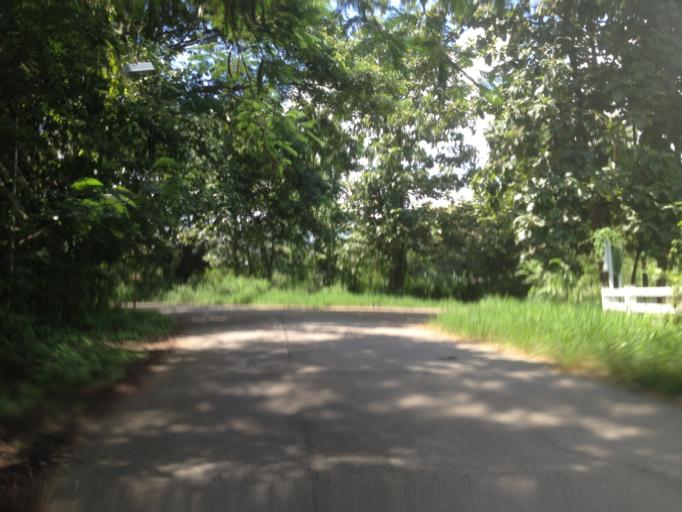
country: TH
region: Chiang Mai
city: Chiang Mai
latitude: 18.7673
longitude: 98.9309
